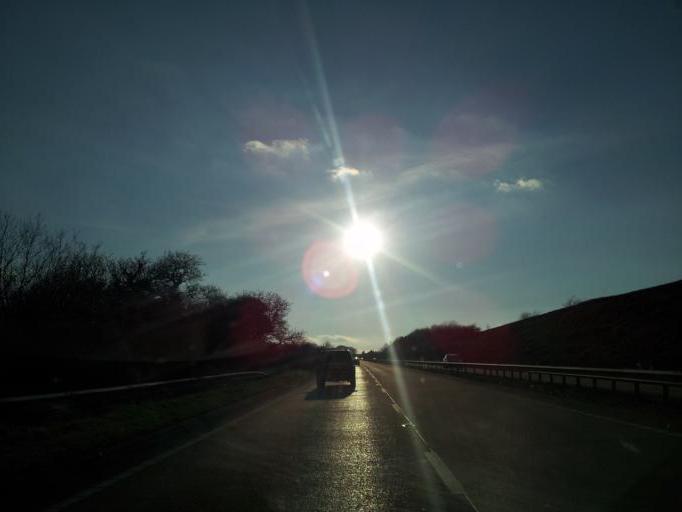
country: GB
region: England
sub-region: Devon
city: Okehampton
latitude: 50.7403
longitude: -3.9372
